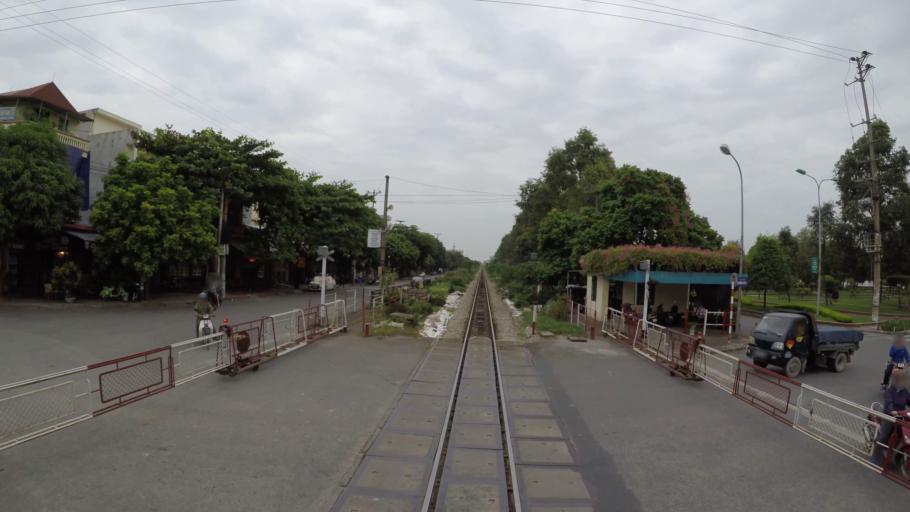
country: VN
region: Hai Duong
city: Thanh Pho Hai Duong
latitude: 20.9441
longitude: 106.3519
